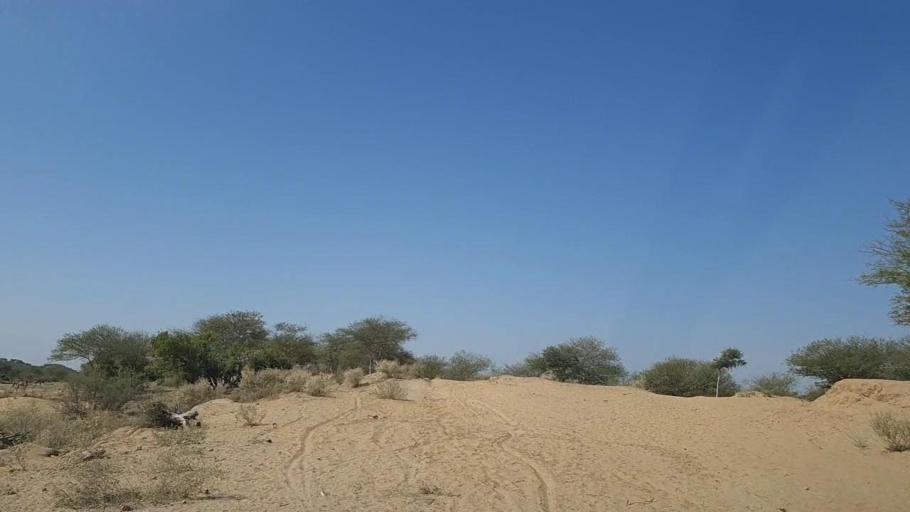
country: PK
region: Sindh
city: Mithi
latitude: 24.7563
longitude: 69.7758
